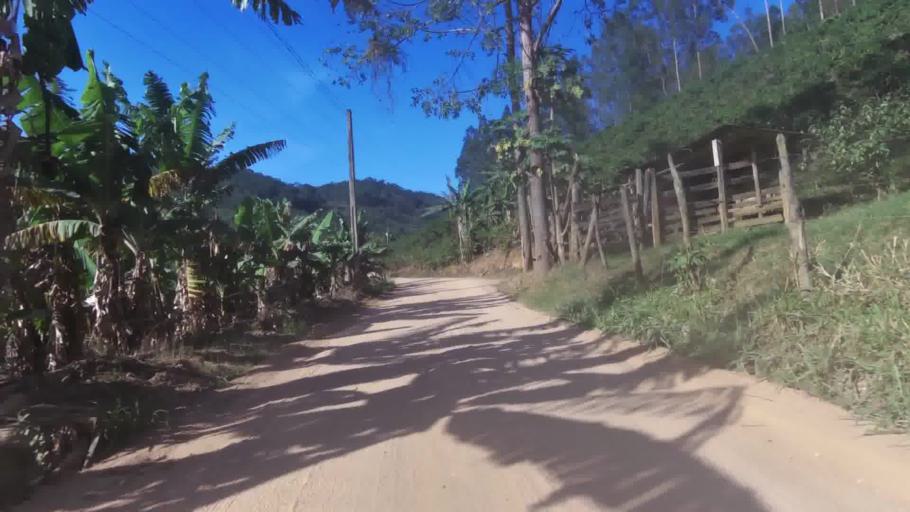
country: BR
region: Espirito Santo
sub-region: Iconha
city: Iconha
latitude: -20.7641
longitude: -40.8305
